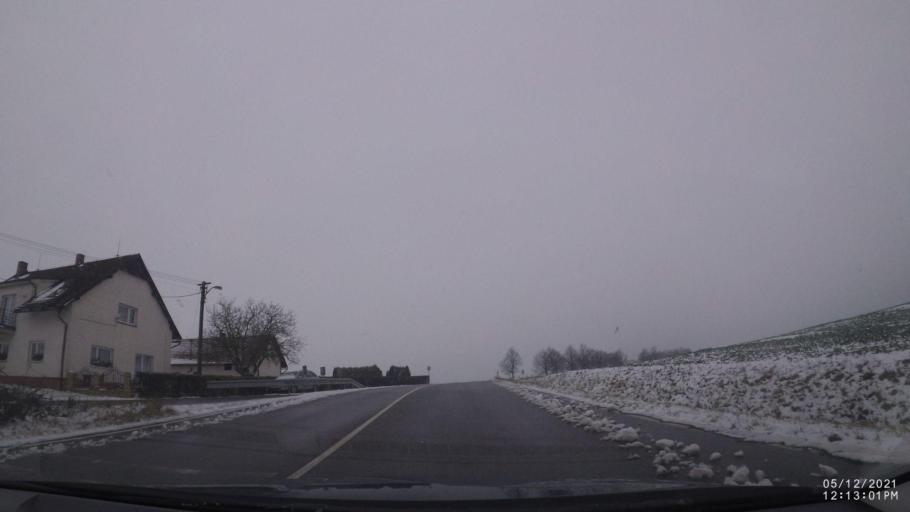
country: CZ
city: Ceske Mezirici
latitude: 50.2973
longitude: 16.0147
